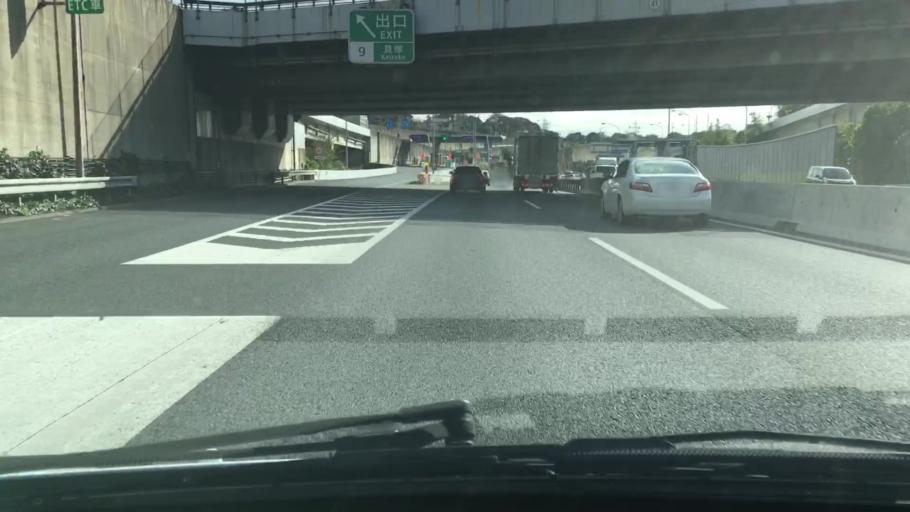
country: JP
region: Chiba
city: Chiba
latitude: 35.6252
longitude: 140.1406
